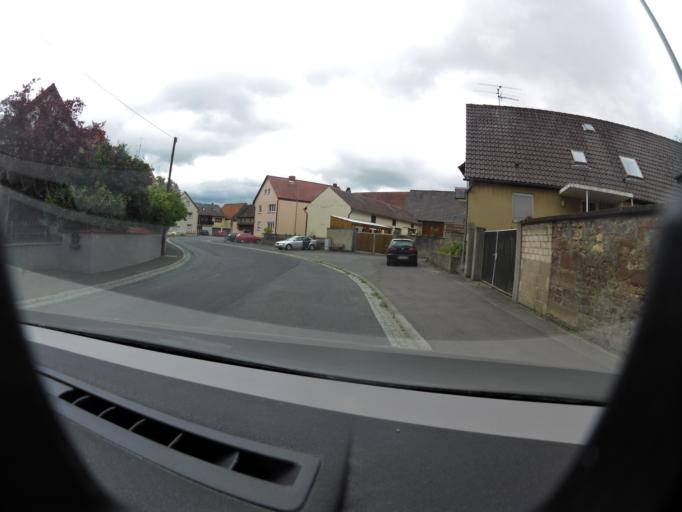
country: DE
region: Bavaria
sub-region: Regierungsbezirk Unterfranken
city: Lulsfeld
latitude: 49.8421
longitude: 10.3025
